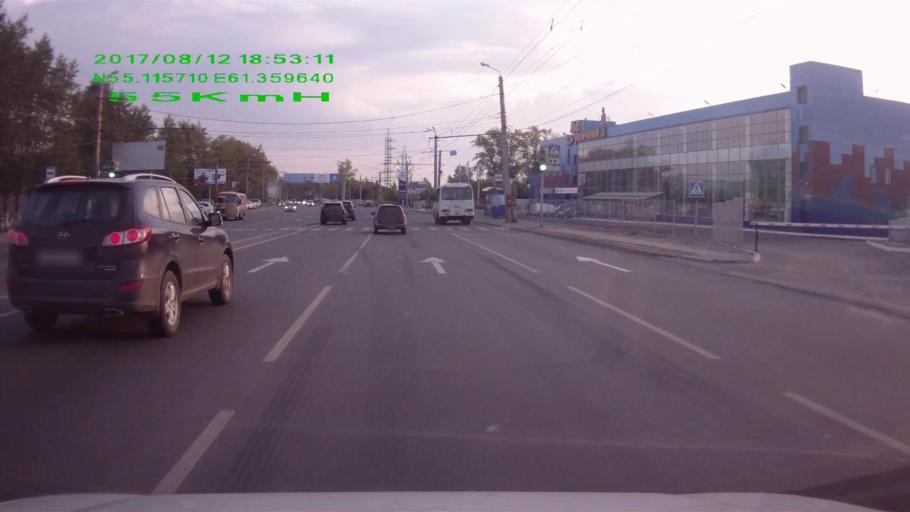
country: RU
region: Chelyabinsk
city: Novosineglazovskiy
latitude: 55.1115
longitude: 61.3561
